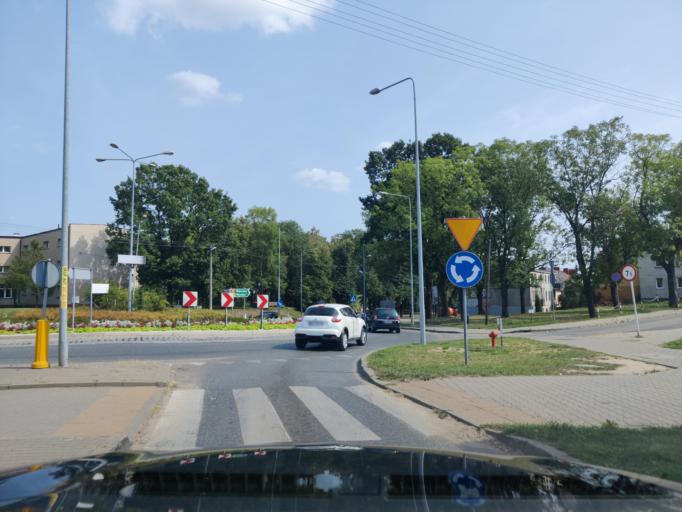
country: PL
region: Masovian Voivodeship
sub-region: Powiat pultuski
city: Pultusk
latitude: 52.7076
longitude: 21.0831
